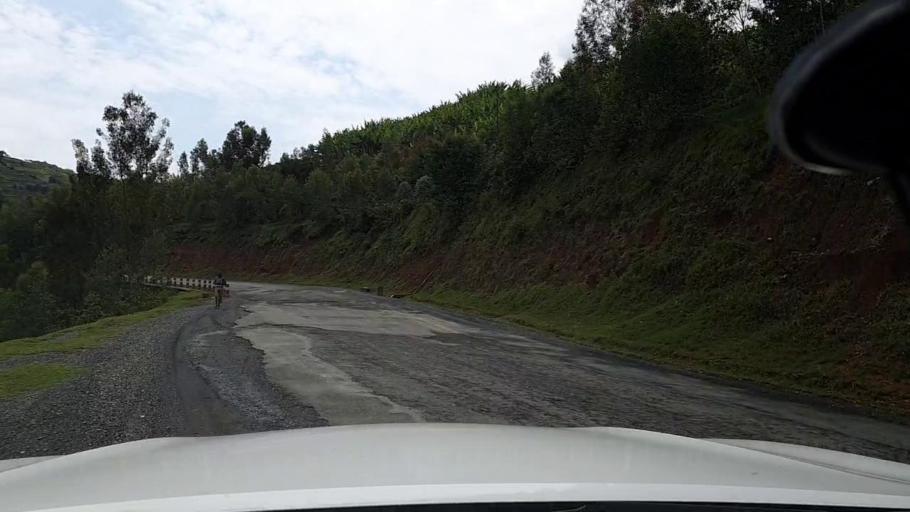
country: RW
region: Southern Province
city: Gitarama
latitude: -2.0611
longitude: 29.5640
